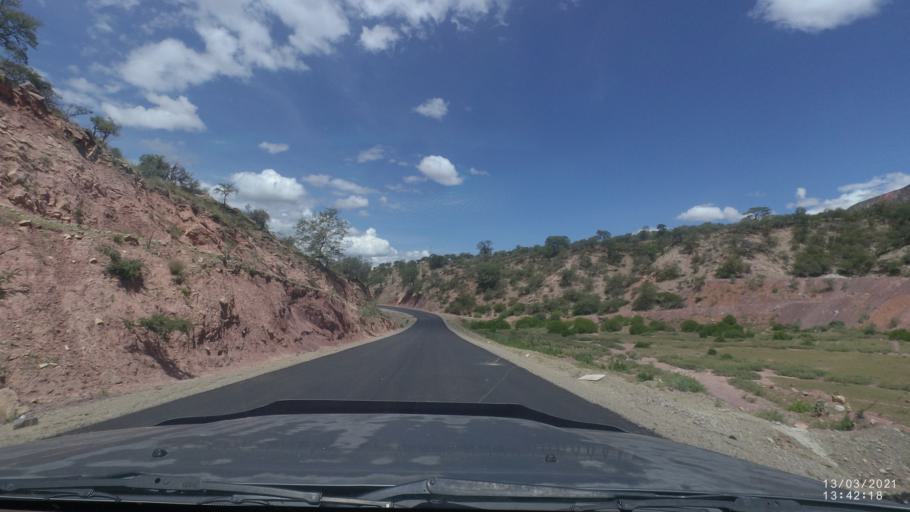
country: BO
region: Cochabamba
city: Cliza
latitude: -17.9135
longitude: -65.8789
